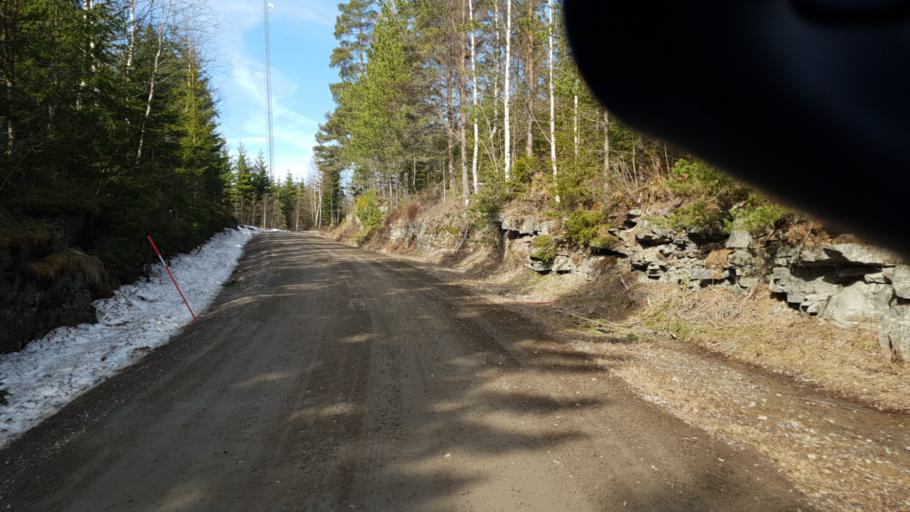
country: SE
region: Vaermland
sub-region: Arvika Kommun
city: Arvika
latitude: 59.5353
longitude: 12.4589
